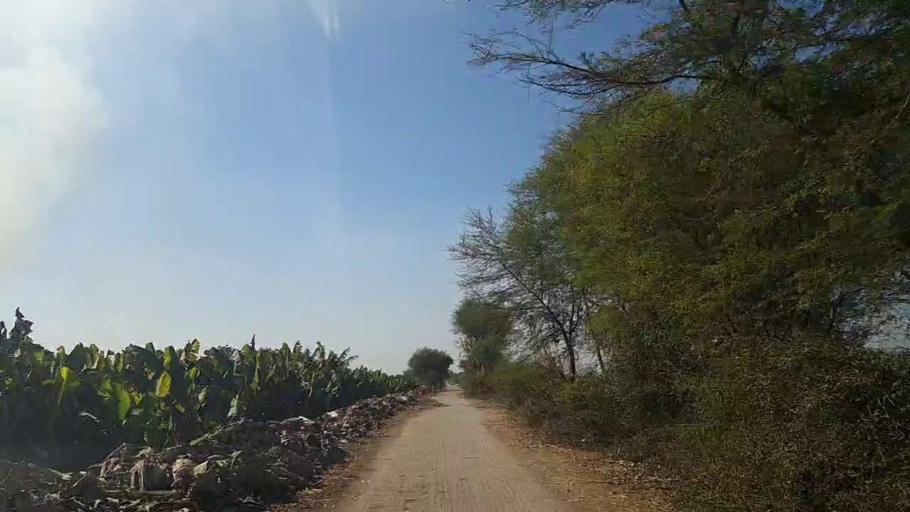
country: PK
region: Sindh
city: Sakrand
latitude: 26.2628
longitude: 68.2193
